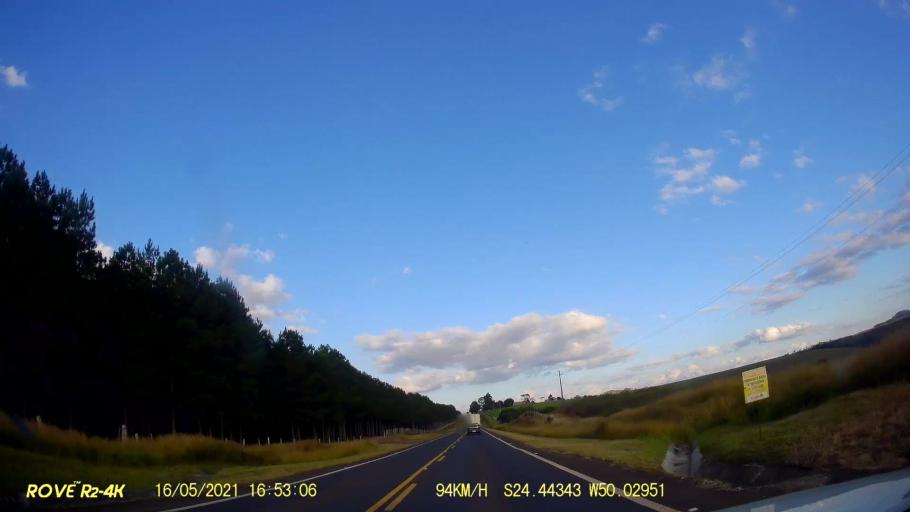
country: BR
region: Parana
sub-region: Pirai Do Sul
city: Pirai do Sul
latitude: -24.4434
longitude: -50.0295
